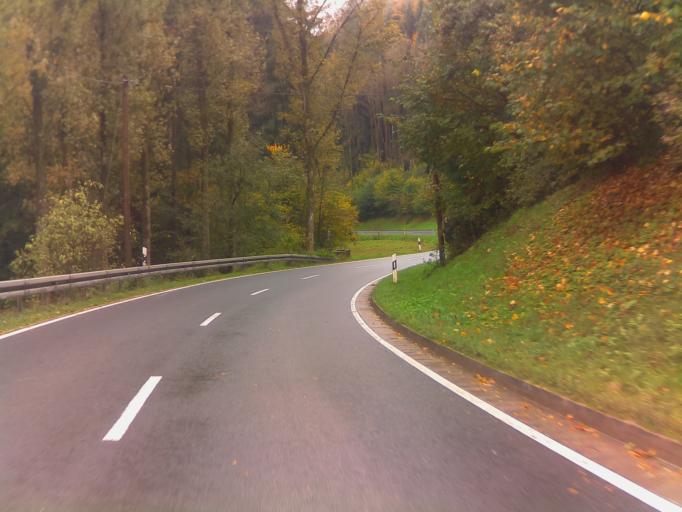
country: DE
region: Bavaria
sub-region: Upper Franconia
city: Wattendorf
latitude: 50.0301
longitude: 11.1156
